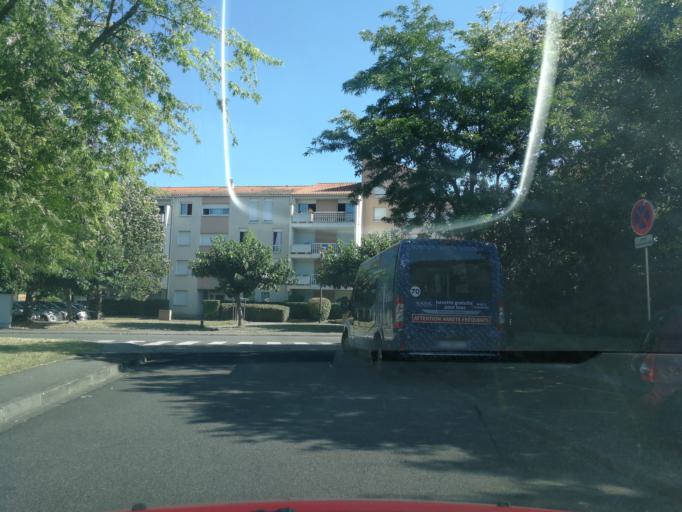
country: FR
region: Midi-Pyrenees
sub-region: Departement de la Haute-Garonne
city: Blagnac
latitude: 43.6343
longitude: 1.3903
